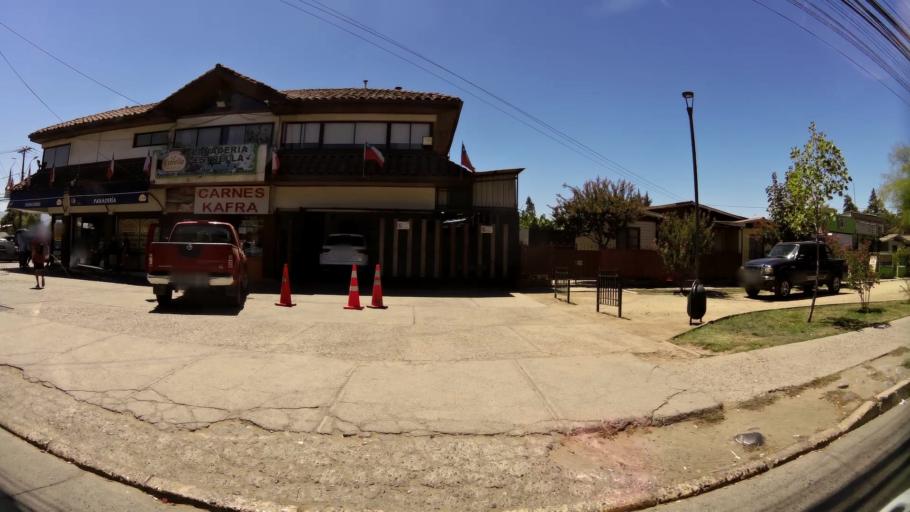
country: CL
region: O'Higgins
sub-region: Provincia de Cachapoal
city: Rancagua
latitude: -34.1674
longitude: -70.7590
